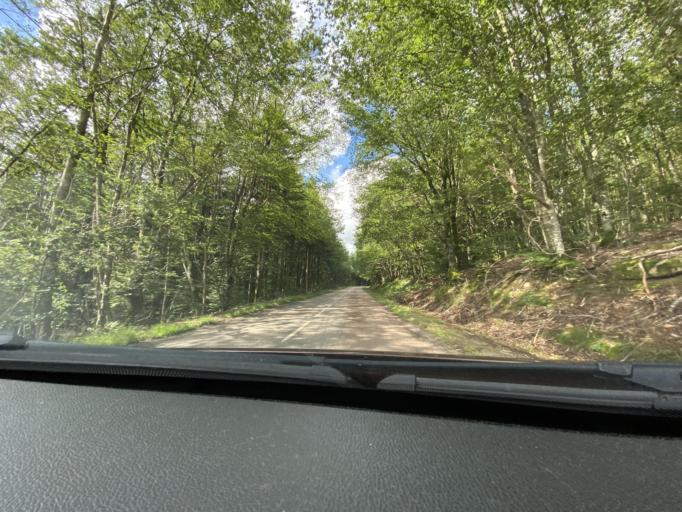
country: FR
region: Bourgogne
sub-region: Departement de la Cote-d'Or
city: Saulieu
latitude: 47.2573
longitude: 4.0713
